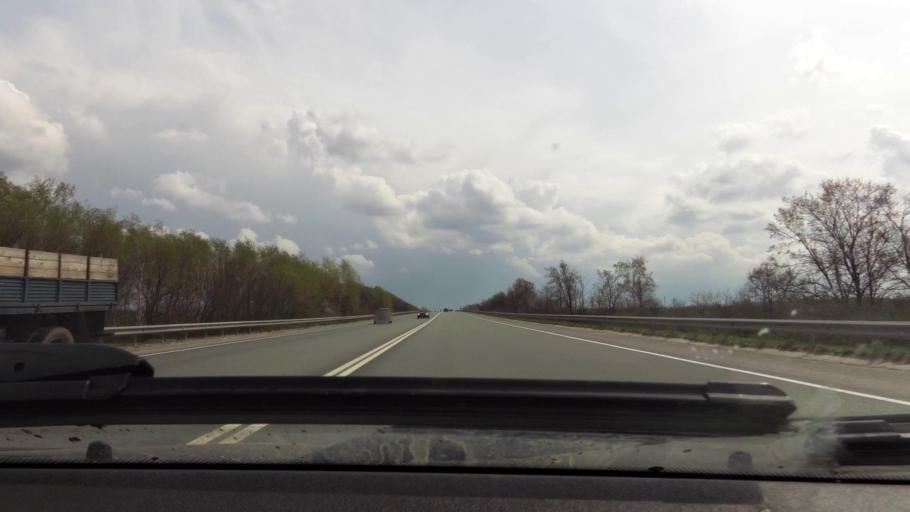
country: RU
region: Rjazan
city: Bagramovo
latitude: 54.7396
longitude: 39.4457
